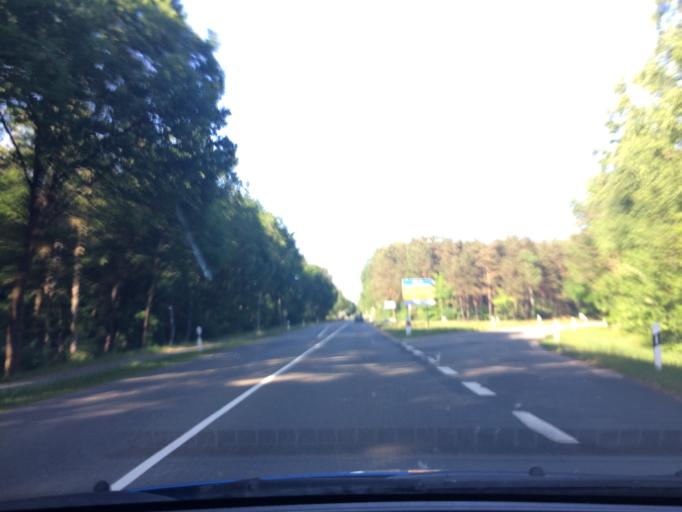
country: DE
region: Lower Saxony
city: Bispingen
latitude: 53.0701
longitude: 9.9694
